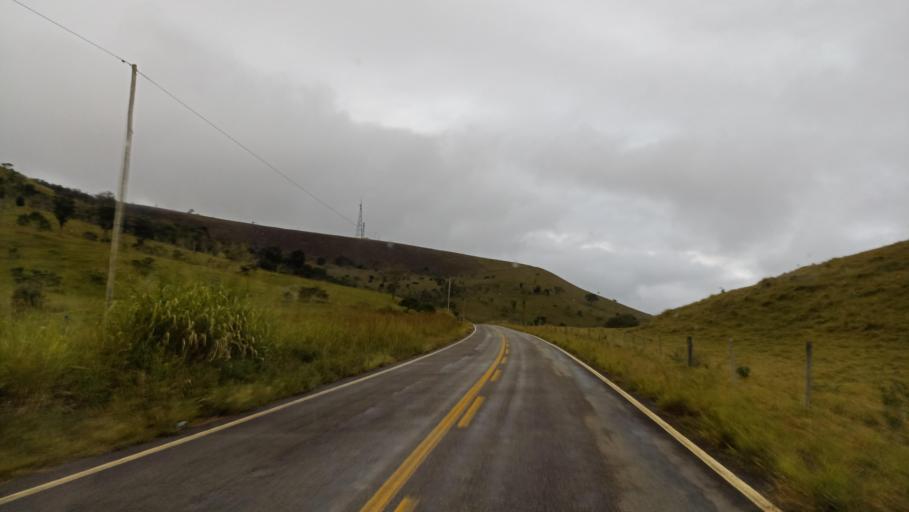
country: BR
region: Minas Gerais
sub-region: Joaima
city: Joaima
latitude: -16.6767
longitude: -40.5250
